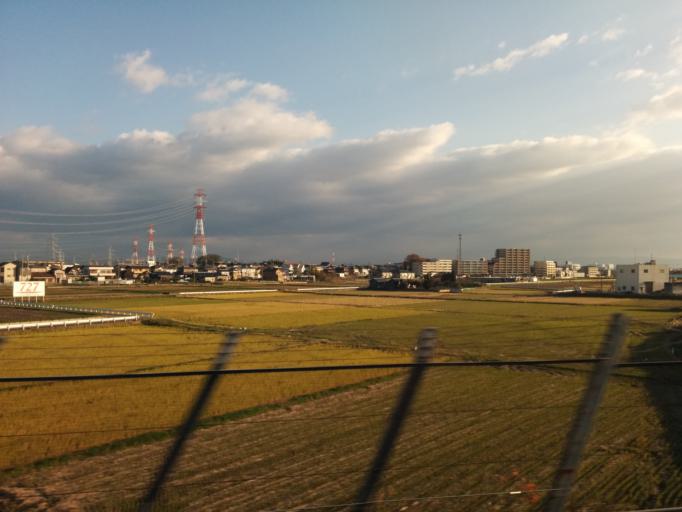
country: JP
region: Aichi
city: Obu
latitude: 35.0186
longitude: 136.9947
